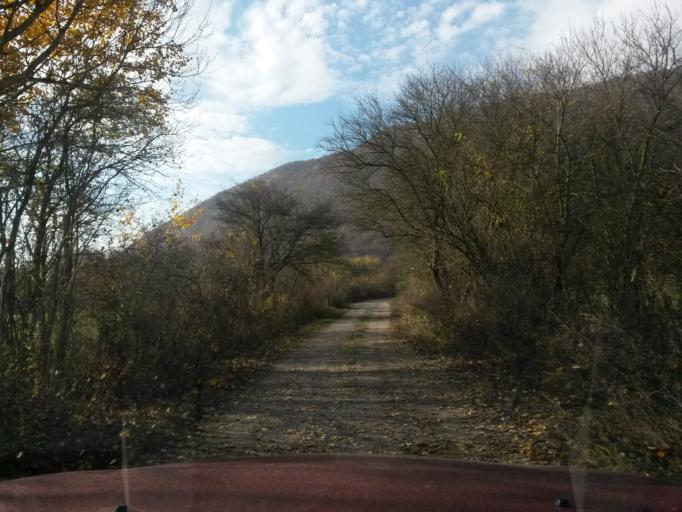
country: SK
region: Kosicky
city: Roznava
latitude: 48.6049
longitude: 20.4805
